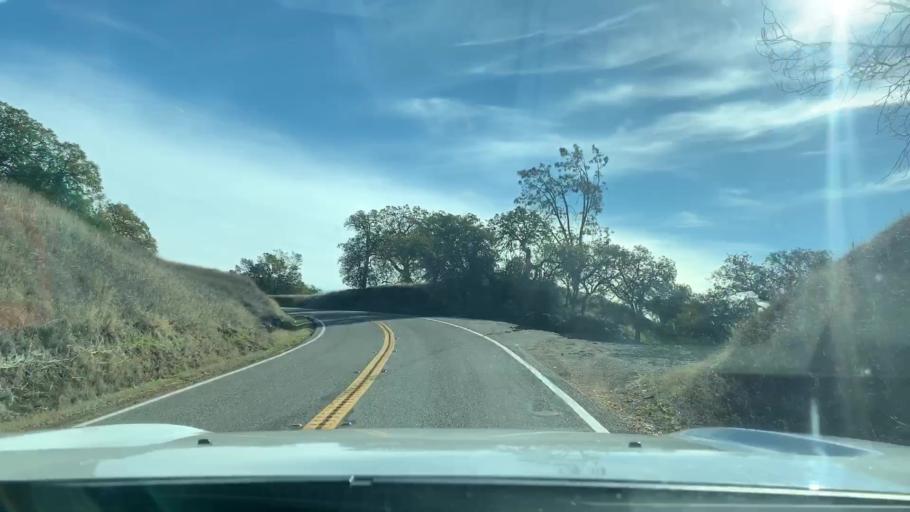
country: US
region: California
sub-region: Monterey County
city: King City
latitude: 36.1926
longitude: -120.7752
